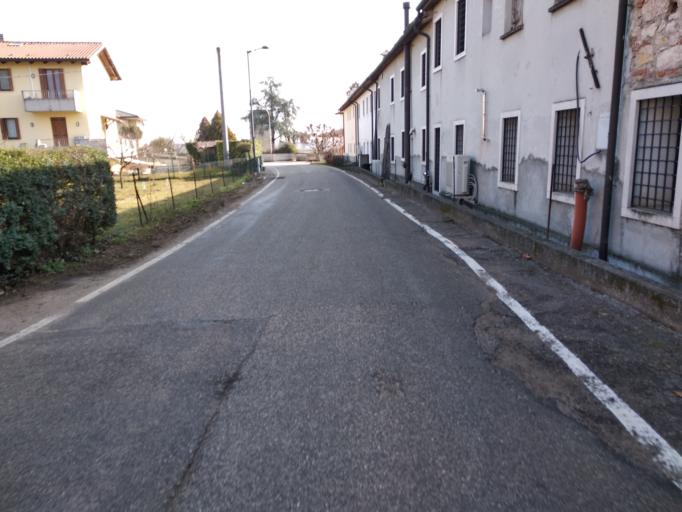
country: IT
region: Veneto
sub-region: Provincia di Vicenza
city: Costabissara
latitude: 45.5930
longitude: 11.4790
